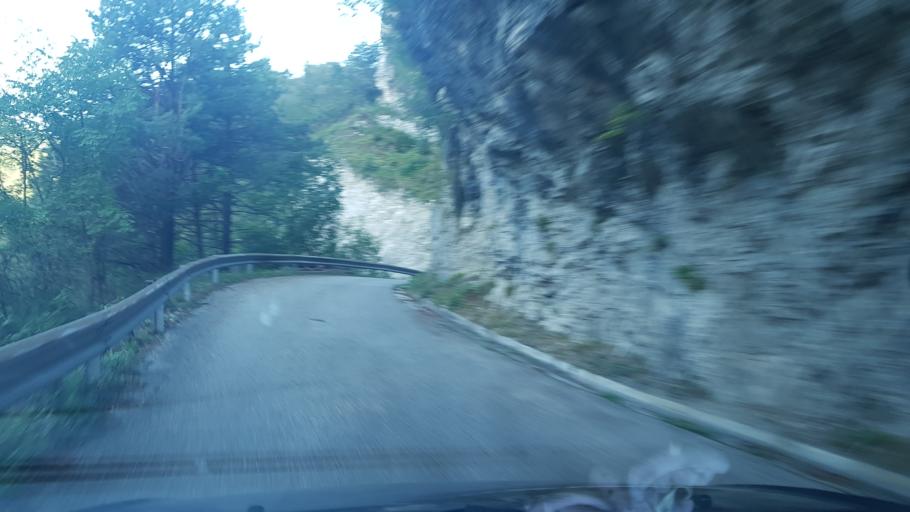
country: IT
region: Friuli Venezia Giulia
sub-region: Provincia di Pordenone
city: Frisanco
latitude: 46.2574
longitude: 12.7252
